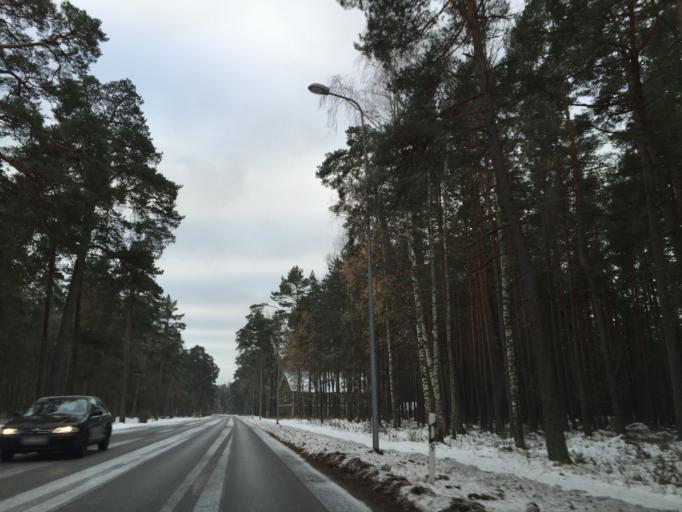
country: LV
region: Saulkrastu
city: Saulkrasti
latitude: 57.2708
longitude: 24.4149
